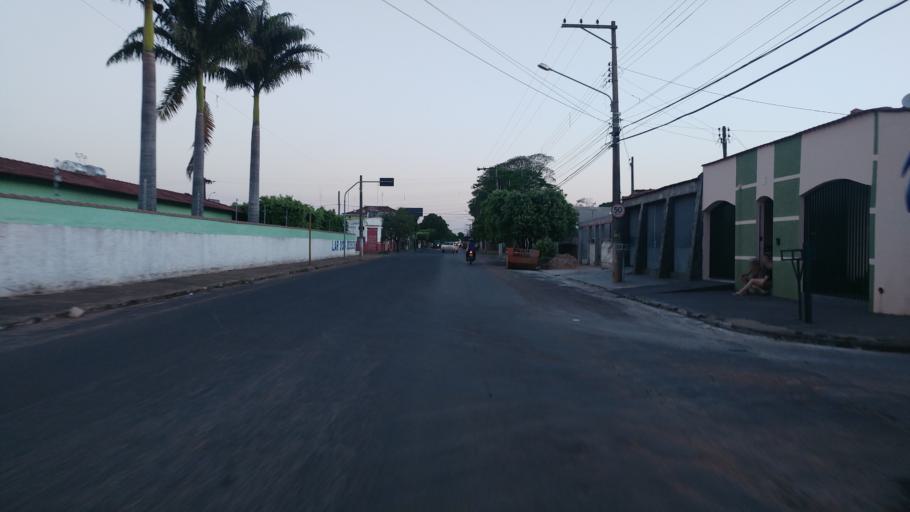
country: BR
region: Sao Paulo
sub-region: Paraguacu Paulista
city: Paraguacu Paulista
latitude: -22.4058
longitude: -50.5709
